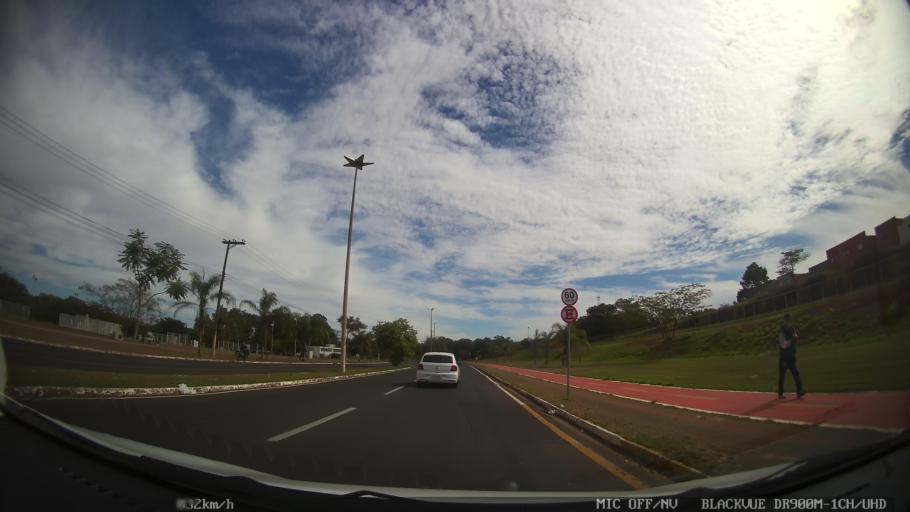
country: BR
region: Sao Paulo
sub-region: Catanduva
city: Catanduva
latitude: -21.1415
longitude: -48.9544
